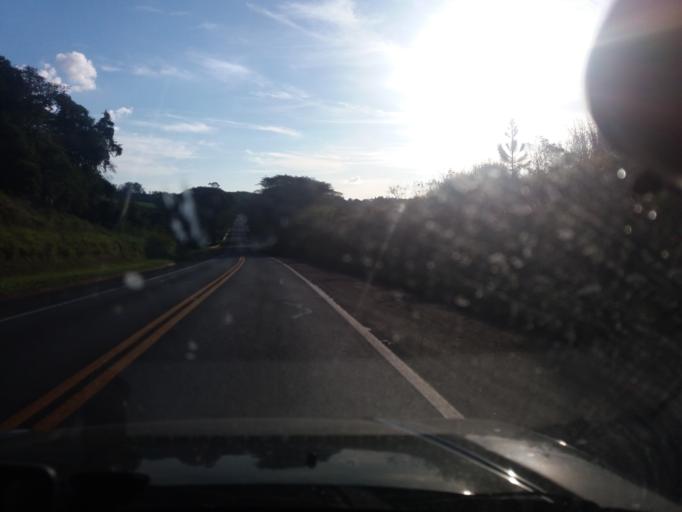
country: BR
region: Sao Paulo
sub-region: Buri
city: Buri
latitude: -23.9284
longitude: -48.6541
